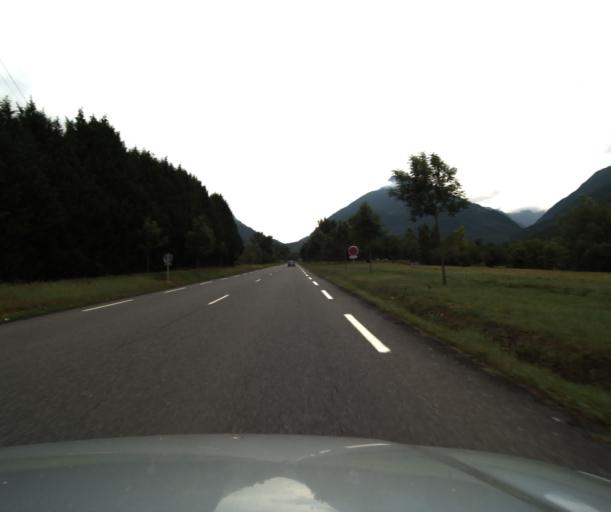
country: FR
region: Midi-Pyrenees
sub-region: Departement des Hautes-Pyrenees
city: Pierrefitte-Nestalas
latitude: 42.9829
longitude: -0.0711
